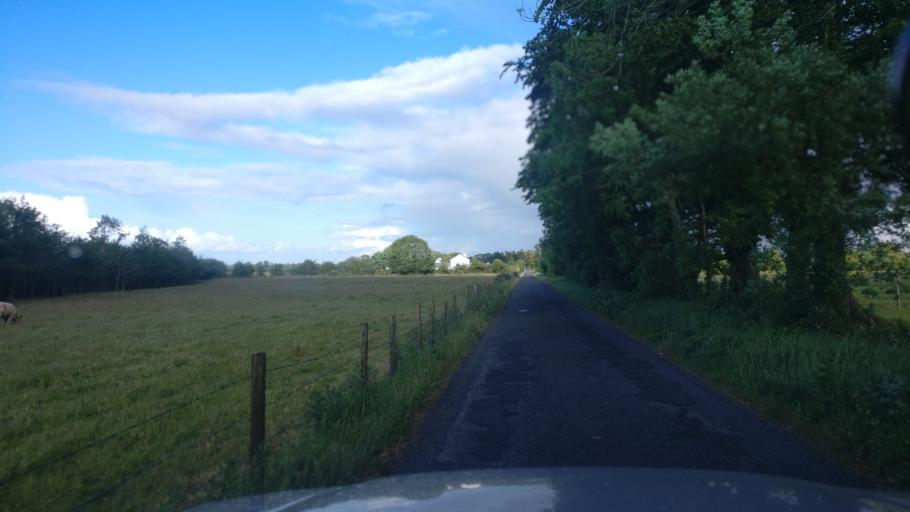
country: IE
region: Connaught
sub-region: County Galway
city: Ballinasloe
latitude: 53.2470
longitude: -8.2206
